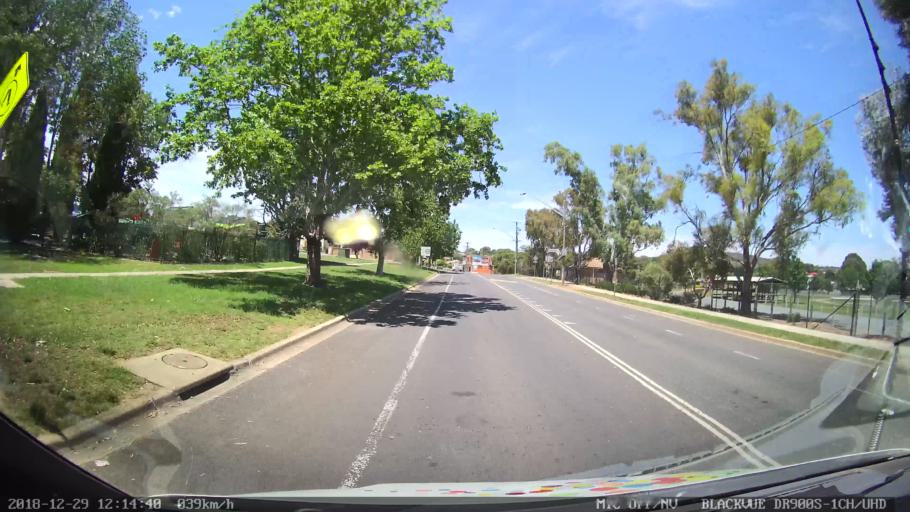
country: AU
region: New South Wales
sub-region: Queanbeyan
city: Queanbeyan
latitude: -35.3568
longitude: 149.2331
